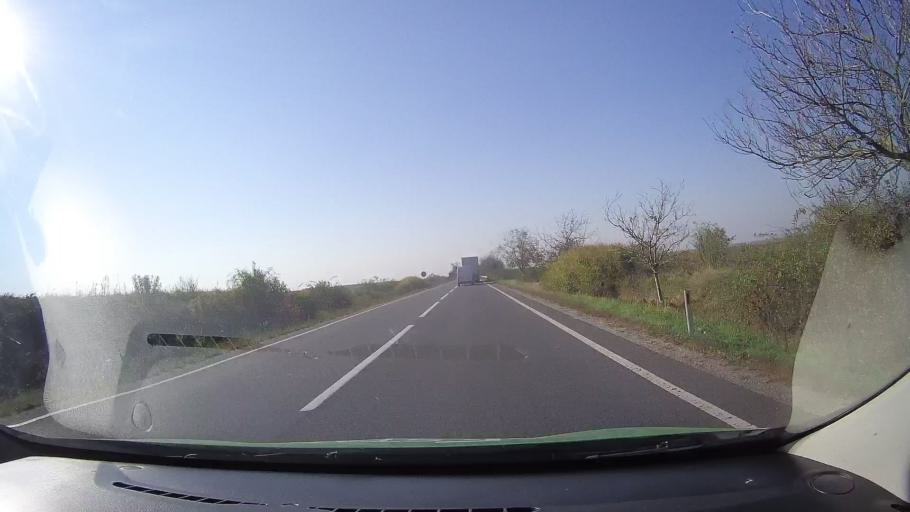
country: RO
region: Satu Mare
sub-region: Comuna Petresti
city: Petresti
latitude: 47.6395
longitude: 22.4038
